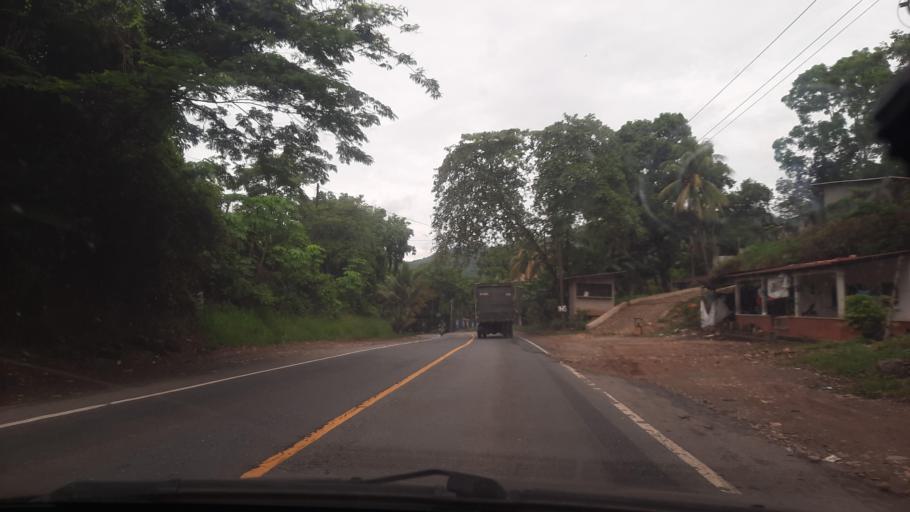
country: GT
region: Izabal
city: Morales
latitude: 15.4621
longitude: -88.9289
